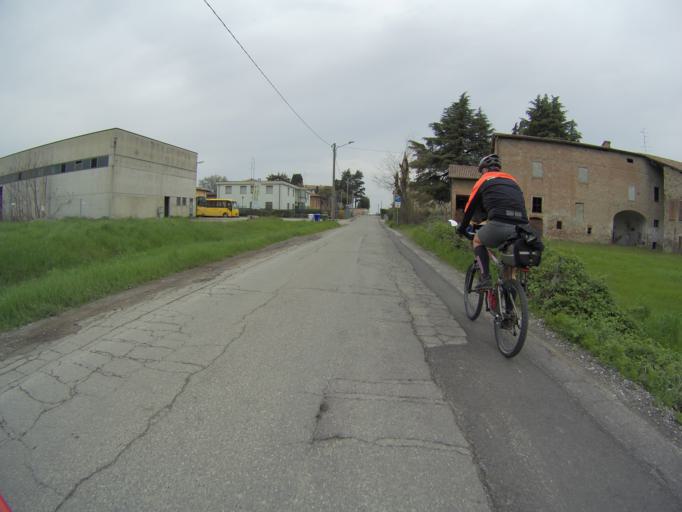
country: IT
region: Emilia-Romagna
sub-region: Provincia di Reggio Emilia
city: Bibbiano
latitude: 44.6586
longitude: 10.4694
